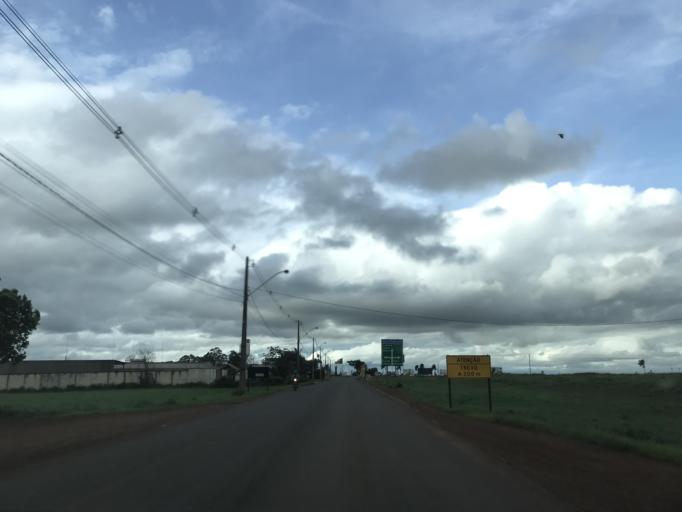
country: BR
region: Goias
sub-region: Vianopolis
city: Vianopolis
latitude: -16.7655
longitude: -48.5219
